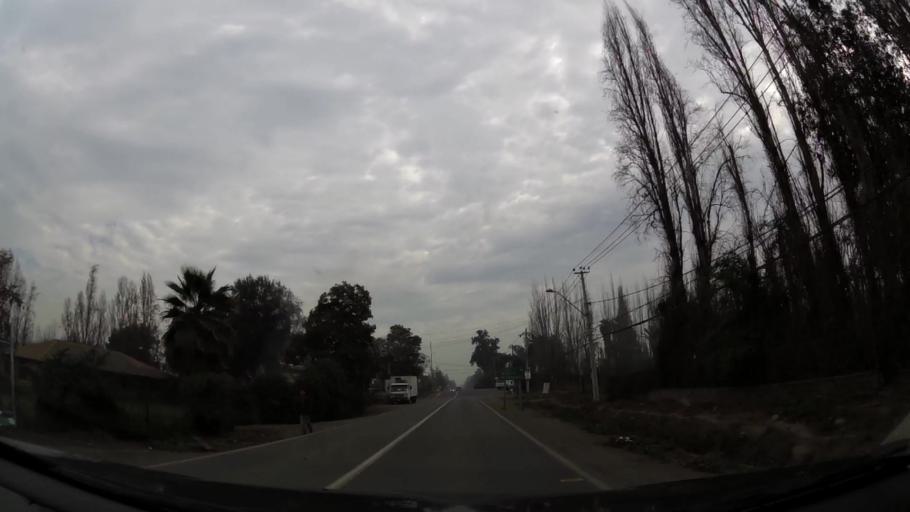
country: CL
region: Santiago Metropolitan
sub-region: Provincia de Chacabuco
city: Lampa
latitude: -33.2435
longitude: -70.7655
